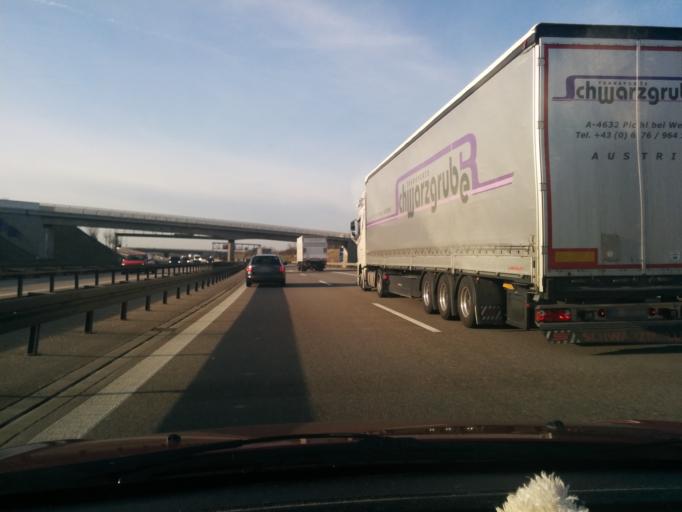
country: DE
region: Bavaria
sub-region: Upper Bavaria
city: Germering
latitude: 48.1507
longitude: 11.3947
